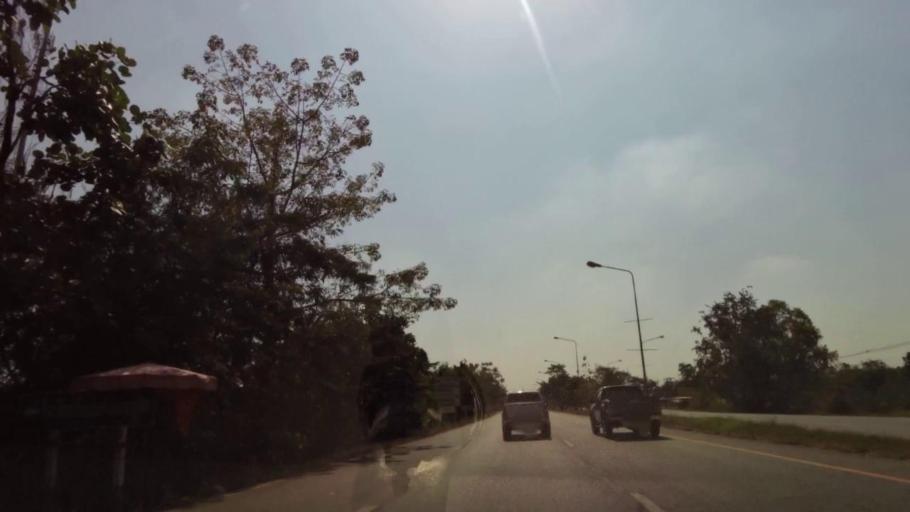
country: TH
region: Phichit
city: Wachira Barami
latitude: 16.4124
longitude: 100.1431
